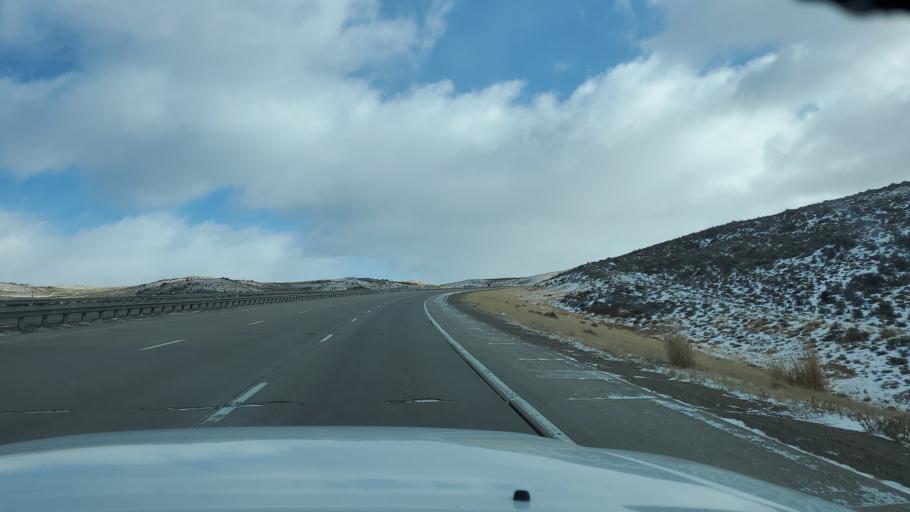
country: US
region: Wyoming
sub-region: Uinta County
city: Evanston
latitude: 41.2731
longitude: -110.8185
